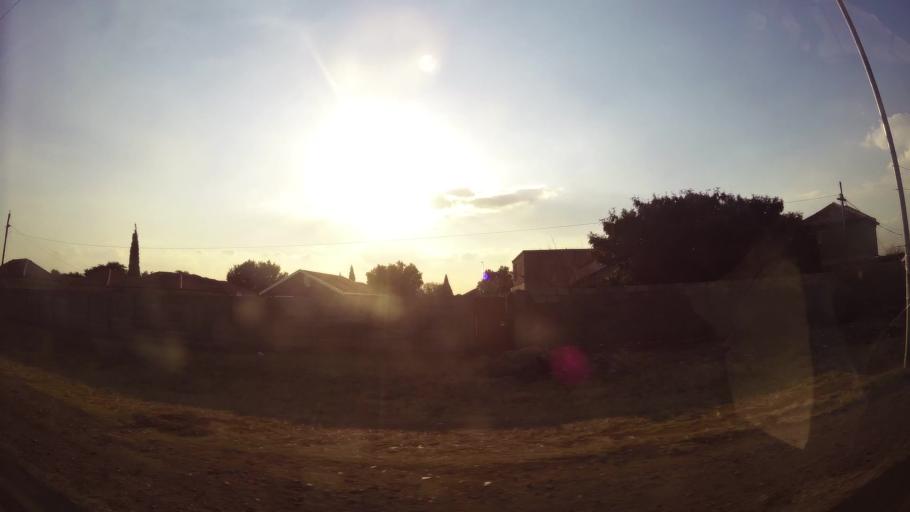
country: ZA
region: Gauteng
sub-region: Ekurhuleni Metropolitan Municipality
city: Boksburg
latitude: -26.3183
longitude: 28.2494
